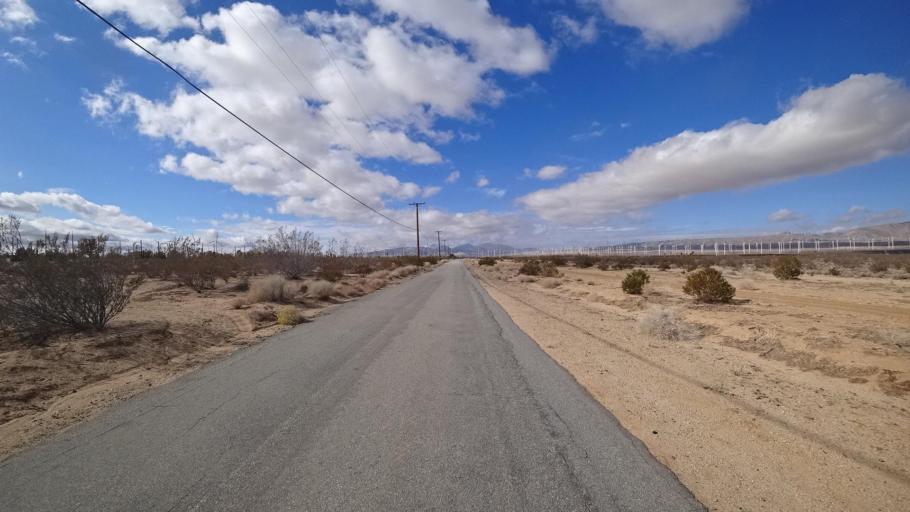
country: US
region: California
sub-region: Kern County
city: Mojave
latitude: 35.0315
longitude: -118.1900
